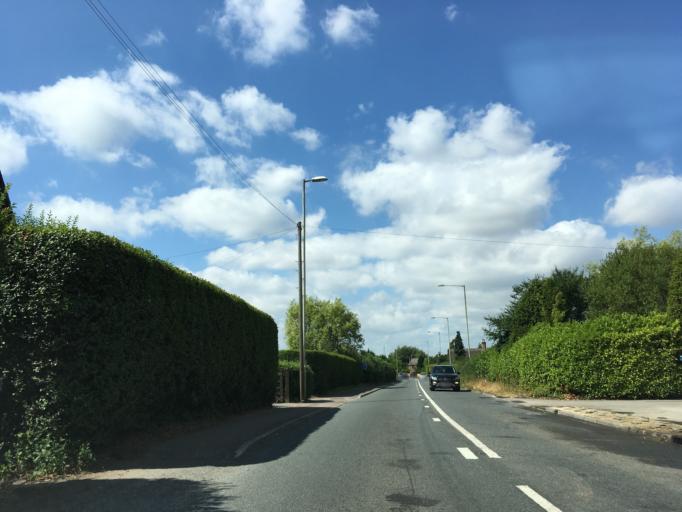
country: GB
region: England
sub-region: Gloucestershire
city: Barnwood
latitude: 51.9011
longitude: -2.2185
